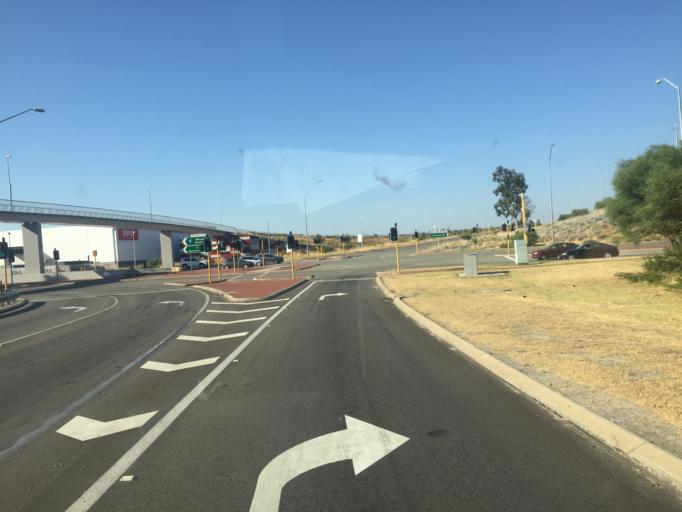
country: AU
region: Western Australia
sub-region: Canning
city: East Cannington
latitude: -32.0039
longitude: 115.9734
